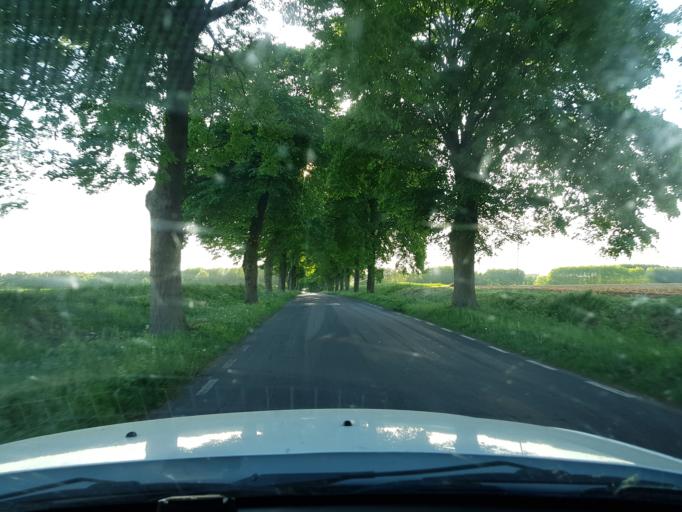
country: PL
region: West Pomeranian Voivodeship
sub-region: Powiat goleniowski
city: Maszewo
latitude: 53.4799
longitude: 15.0043
